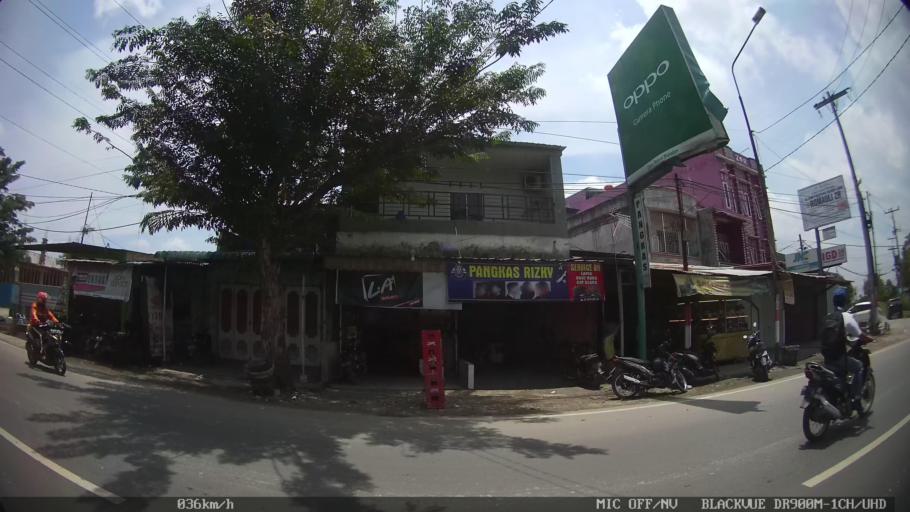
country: ID
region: North Sumatra
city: Labuhan Deli
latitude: 3.7172
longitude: 98.6640
